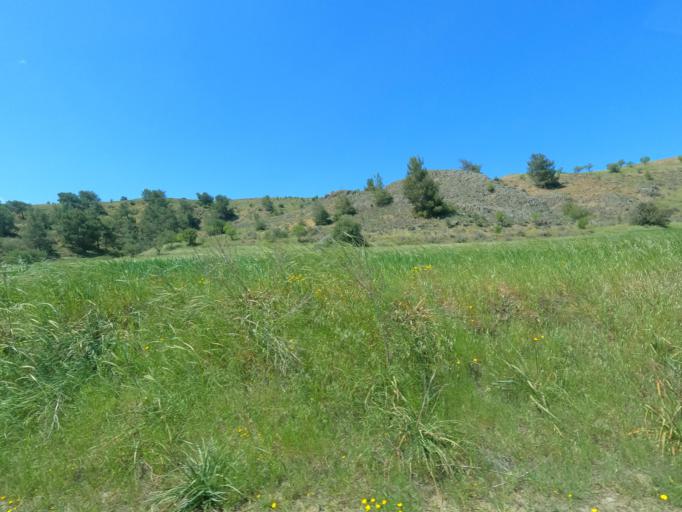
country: CY
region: Lefkosia
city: Peristerona
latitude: 35.0495
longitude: 33.0767
